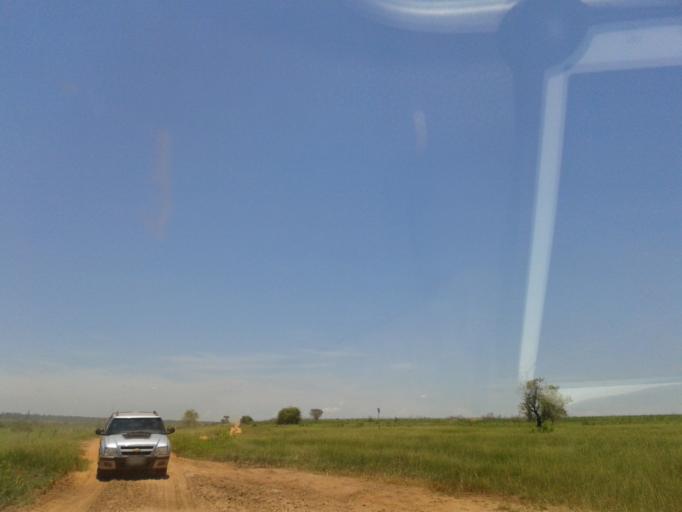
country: BR
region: Minas Gerais
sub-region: Santa Vitoria
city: Santa Vitoria
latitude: -19.2188
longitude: -50.4312
